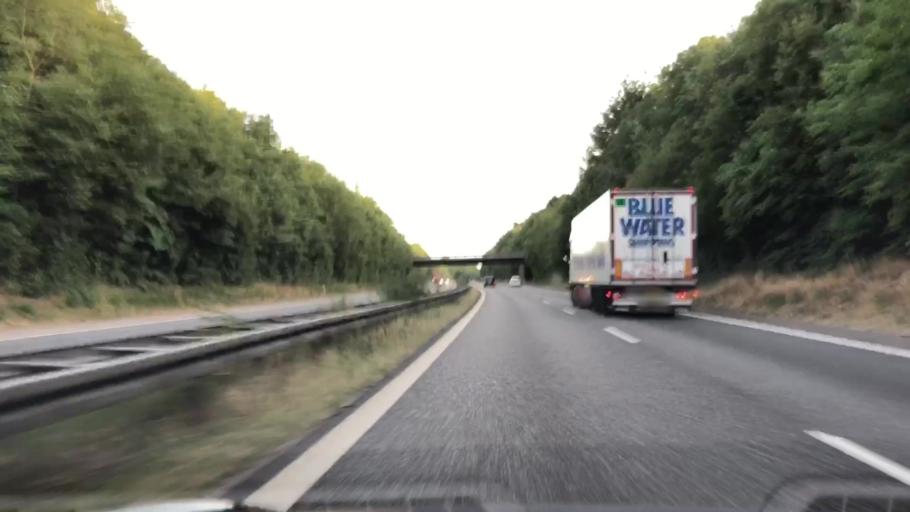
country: DK
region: South Denmark
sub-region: Haderslev Kommune
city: Vojens
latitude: 55.2293
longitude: 9.3810
